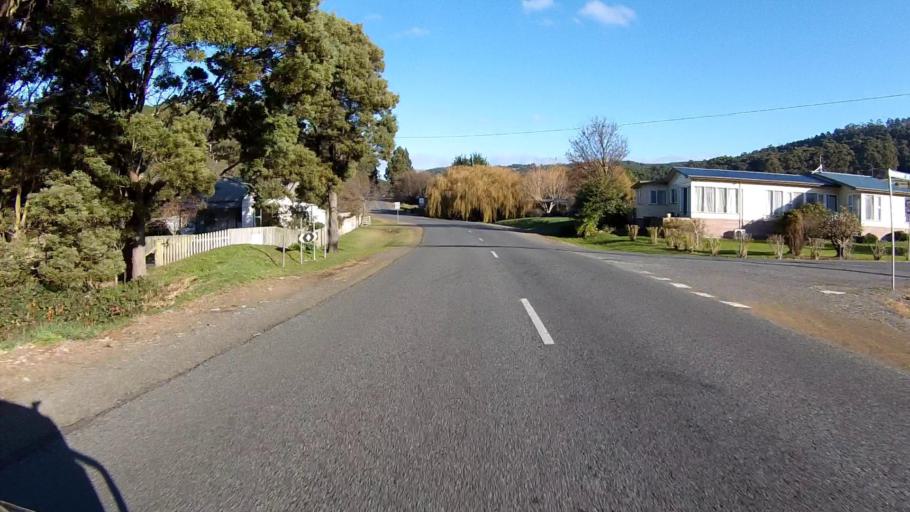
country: AU
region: Tasmania
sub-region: Clarence
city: Sandford
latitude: -43.1464
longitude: 147.8438
